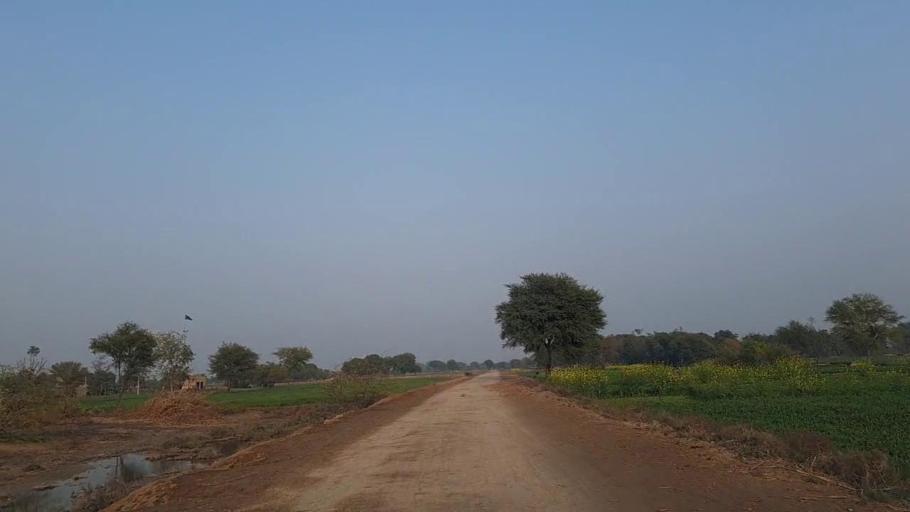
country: PK
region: Sindh
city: Nawabshah
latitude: 26.2510
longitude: 68.4704
